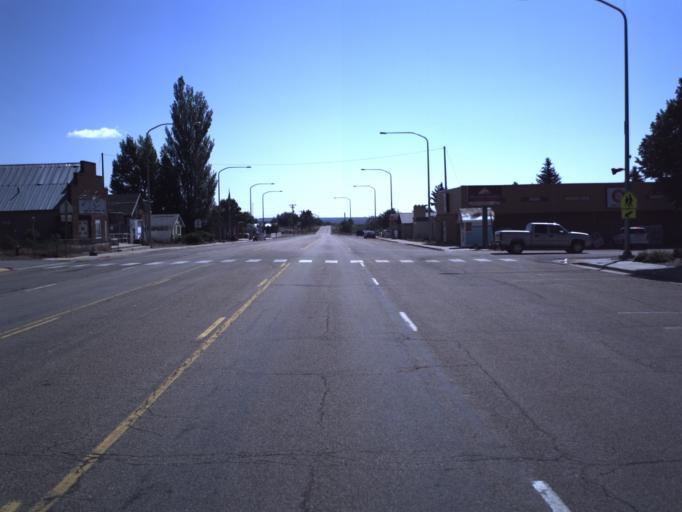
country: US
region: Utah
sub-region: Duchesne County
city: Duchesne
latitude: 40.3592
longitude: -110.2884
